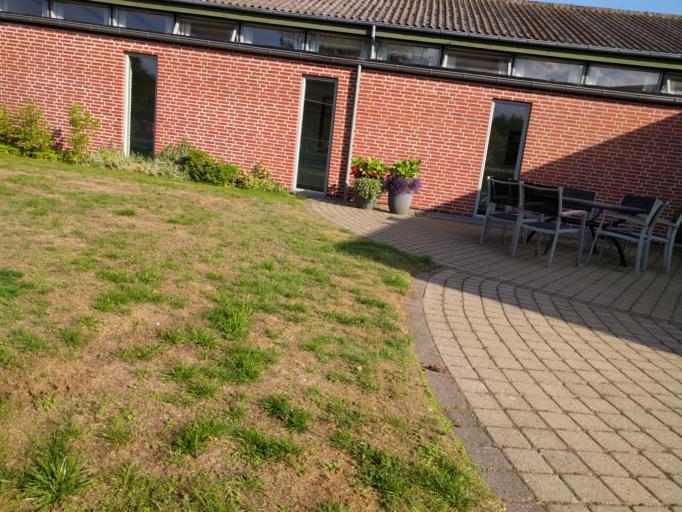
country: DK
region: Central Jutland
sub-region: Skive Kommune
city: Hojslev
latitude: 56.6042
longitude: 9.2843
